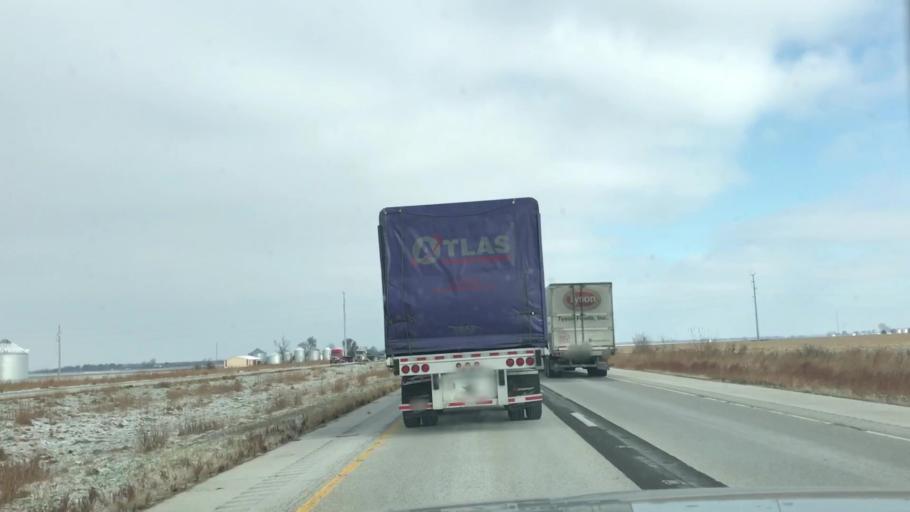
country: US
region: Illinois
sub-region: Sangamon County
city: Divernon
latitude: 39.5266
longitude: -89.6456
